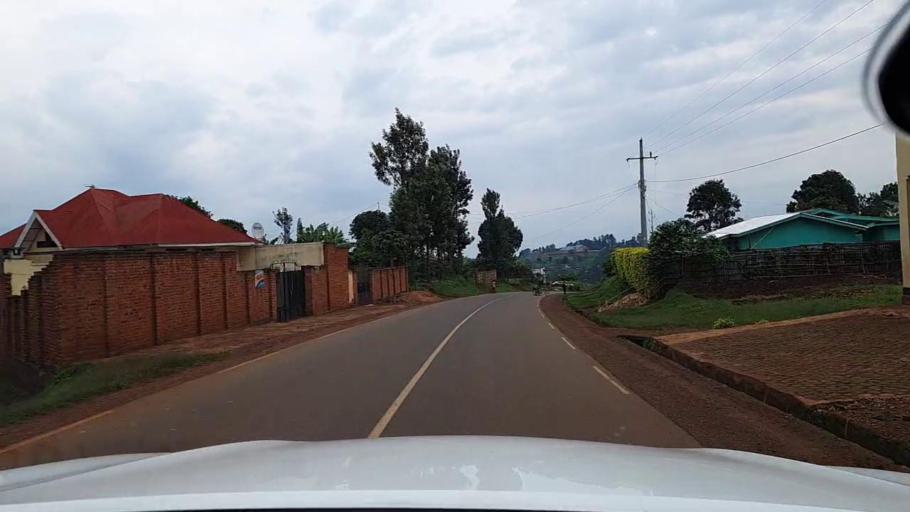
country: RW
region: Western Province
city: Cyangugu
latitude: -2.6282
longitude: 28.9511
